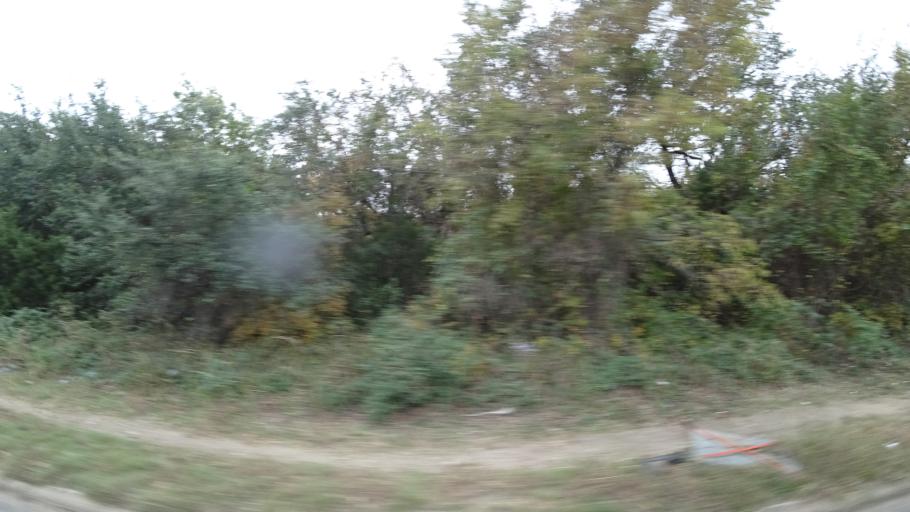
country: US
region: Texas
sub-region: Williamson County
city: Anderson Mill
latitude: 30.4751
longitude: -97.8142
